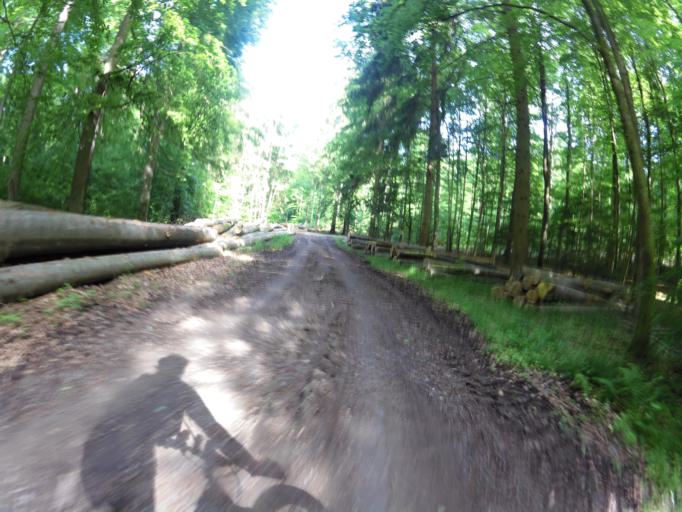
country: DE
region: Bavaria
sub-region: Regierungsbezirk Unterfranken
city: Uettingen
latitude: 49.7746
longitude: 9.7524
